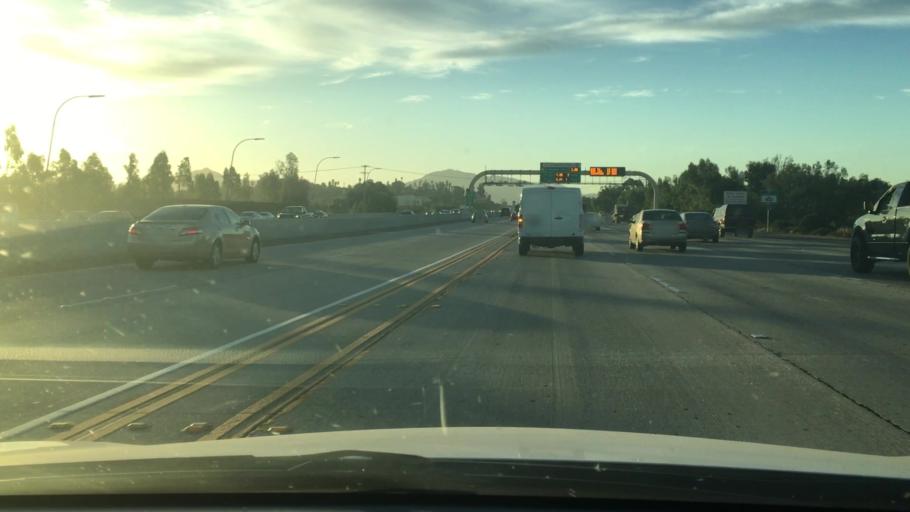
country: US
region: California
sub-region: San Diego County
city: Escondido
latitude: 33.0955
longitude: -117.0861
